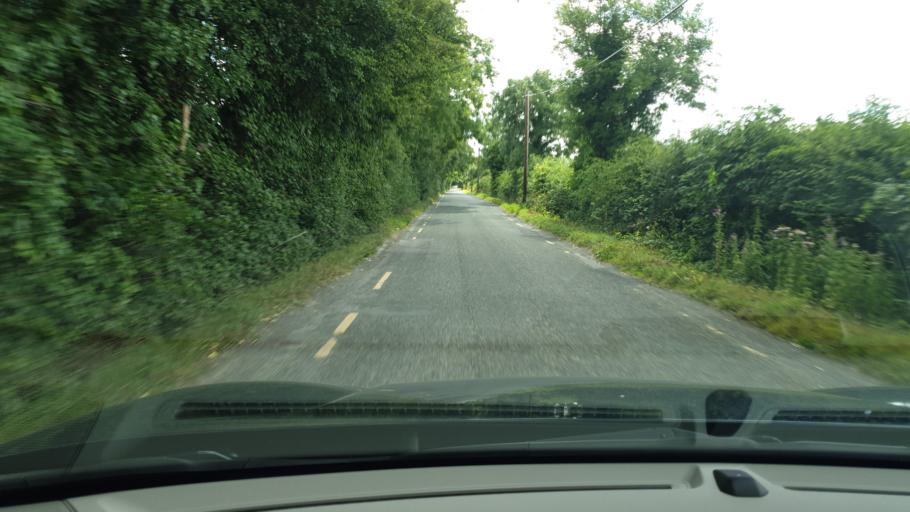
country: IE
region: Leinster
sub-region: An Mhi
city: Dunboyne
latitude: 53.3854
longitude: -6.4699
